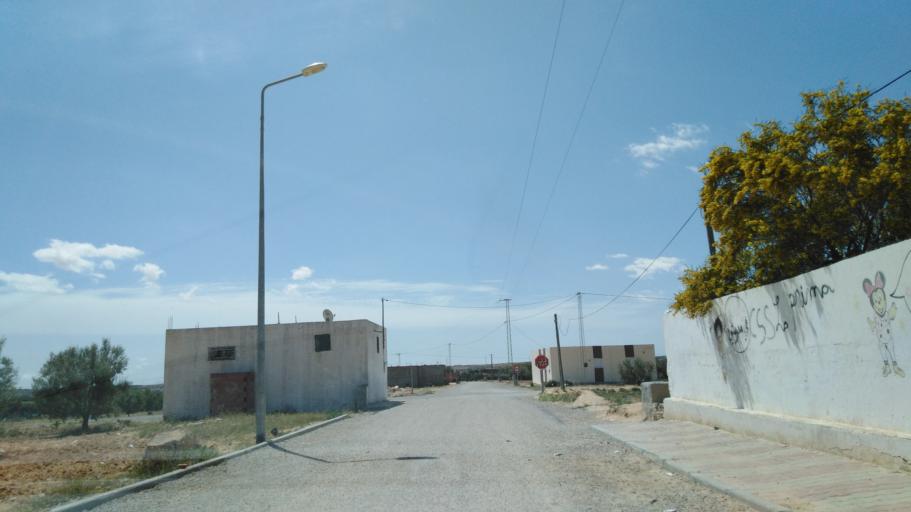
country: TN
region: Safaqis
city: Sfax
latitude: 34.7451
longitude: 10.5514
